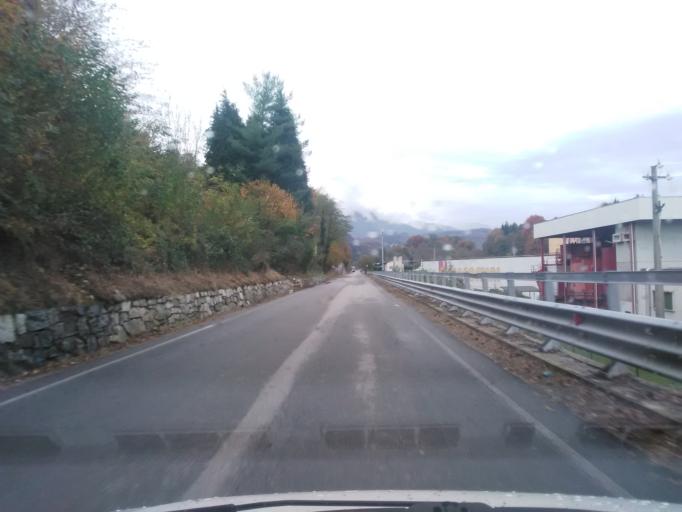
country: IT
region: Piedmont
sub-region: Provincia di Novara
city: San Maurizio D'Opaglio
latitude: 45.7791
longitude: 8.3845
